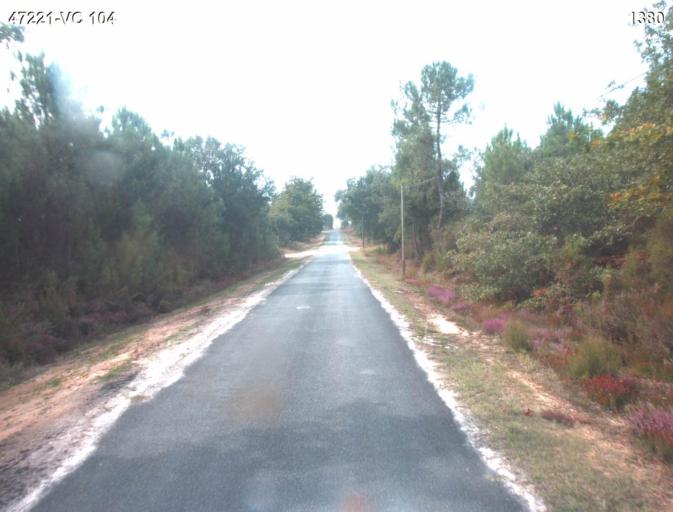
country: FR
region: Aquitaine
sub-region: Departement du Lot-et-Garonne
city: Mezin
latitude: 44.1252
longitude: 0.2116
